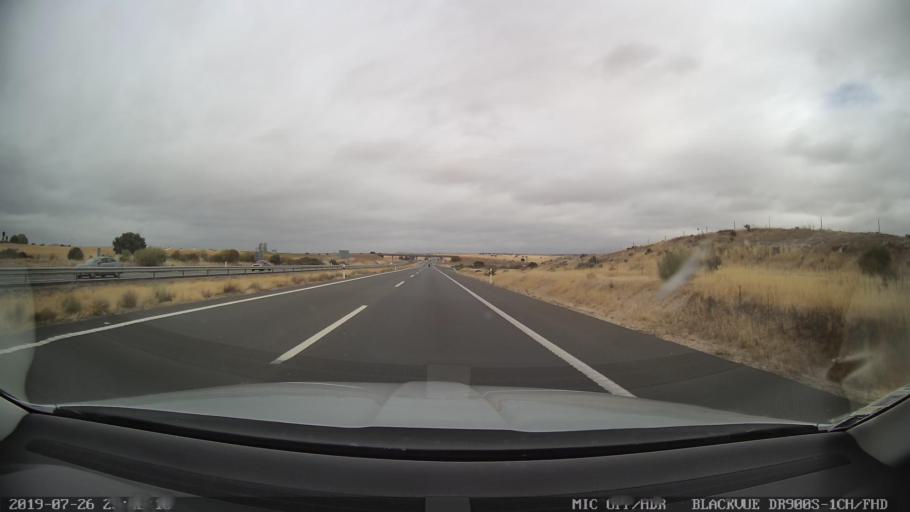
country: ES
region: Extremadura
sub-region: Provincia de Caceres
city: Trujillo
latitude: 39.4992
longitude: -5.8402
